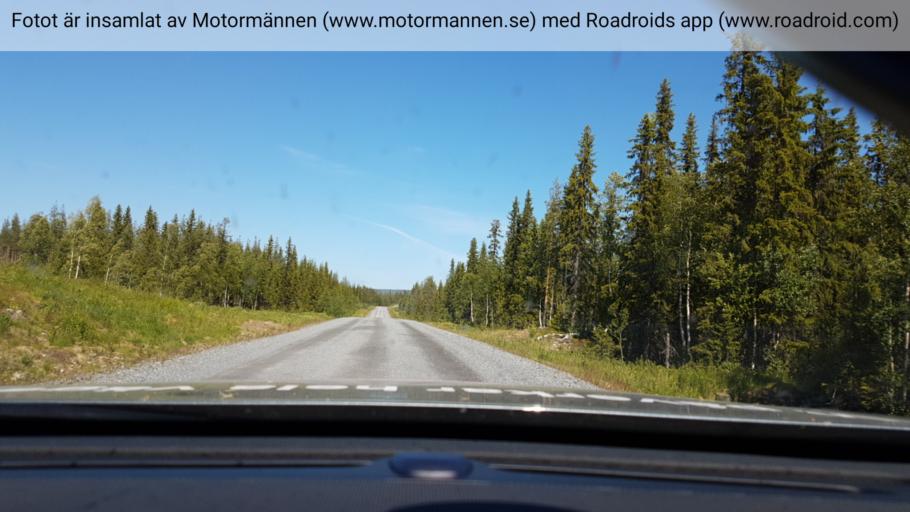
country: SE
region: Vaesterbotten
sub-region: Vilhelmina Kommun
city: Sjoberg
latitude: 64.6930
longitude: 15.7572
